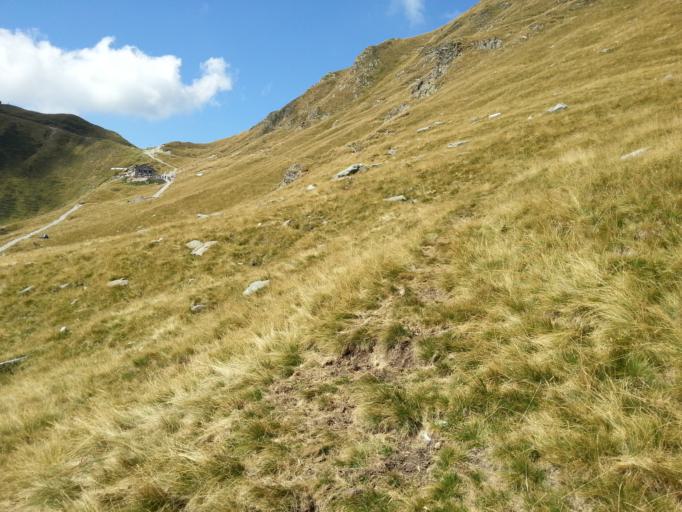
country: CH
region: Grisons
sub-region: Moesa District
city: Roveredo
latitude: 46.1677
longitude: 9.1649
